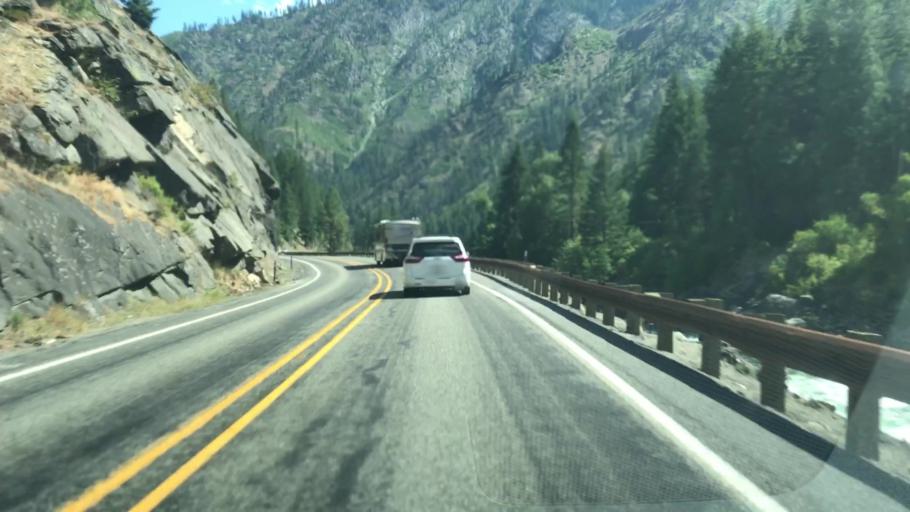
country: US
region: Washington
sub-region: Chelan County
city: Leavenworth
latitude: 47.5938
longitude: -120.7122
